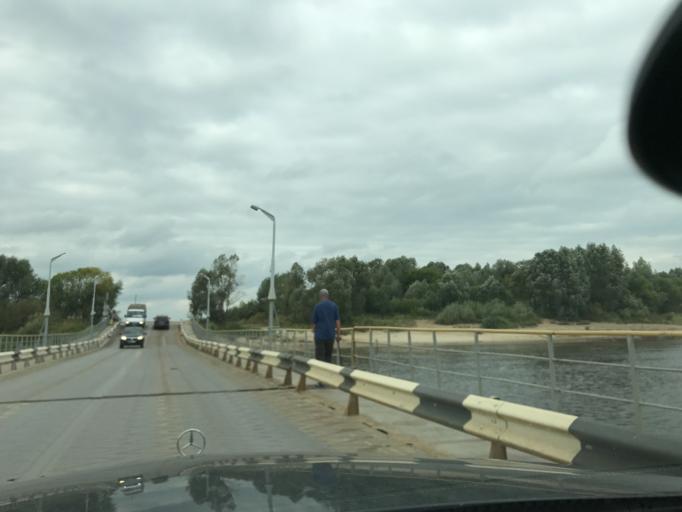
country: RU
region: Nizjnij Novgorod
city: Pavlovo
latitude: 55.9709
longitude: 43.0641
